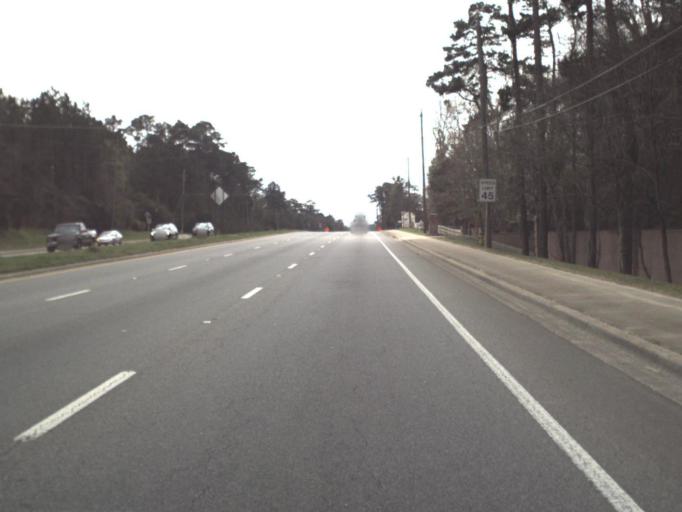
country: US
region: Florida
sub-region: Leon County
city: Tallahassee
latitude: 30.5550
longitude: -84.2218
